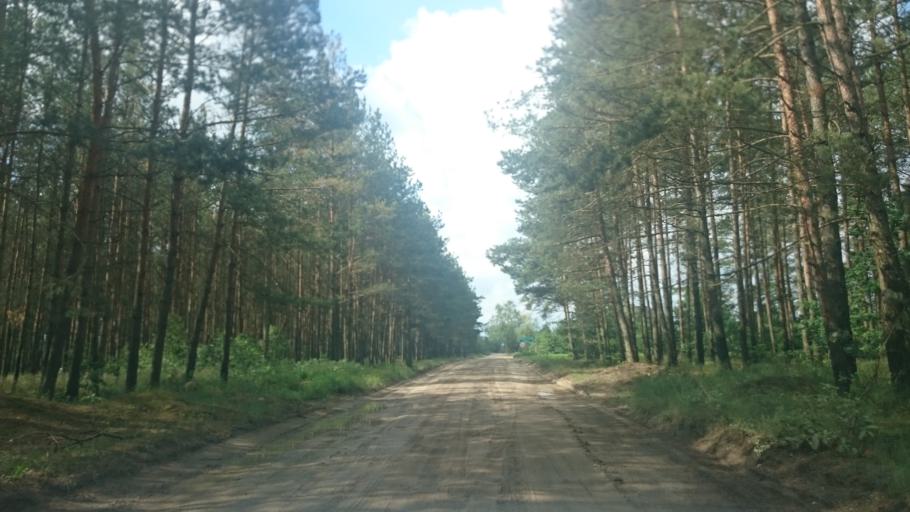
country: PL
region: Pomeranian Voivodeship
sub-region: Powiat koscierski
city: Karsin
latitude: 53.9778
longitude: 17.9318
